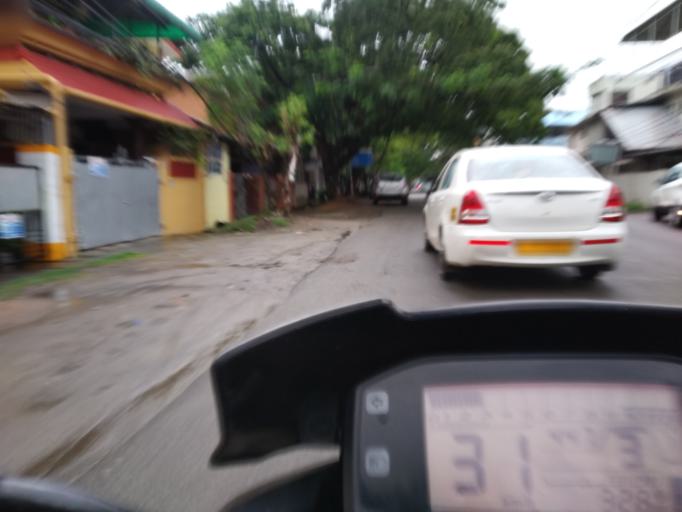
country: IN
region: Kerala
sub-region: Ernakulam
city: Cochin
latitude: 9.9774
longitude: 76.2937
